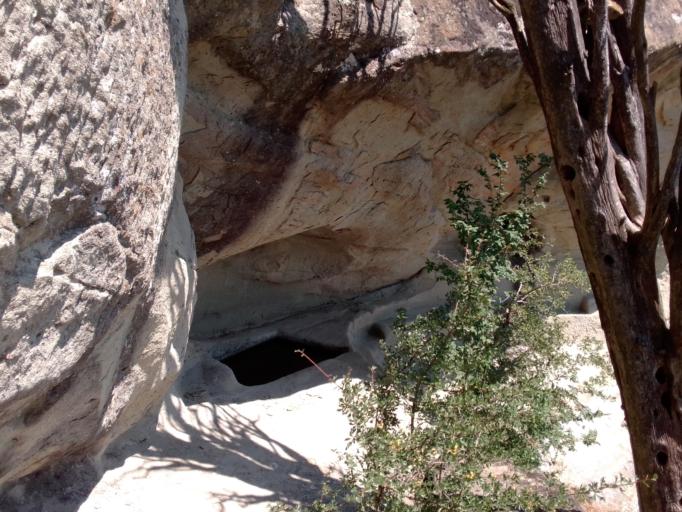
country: IT
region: Emilia-Romagna
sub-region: Provincia di Piacenza
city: Pianello Val Tidone
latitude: 44.9123
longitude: 9.3942
